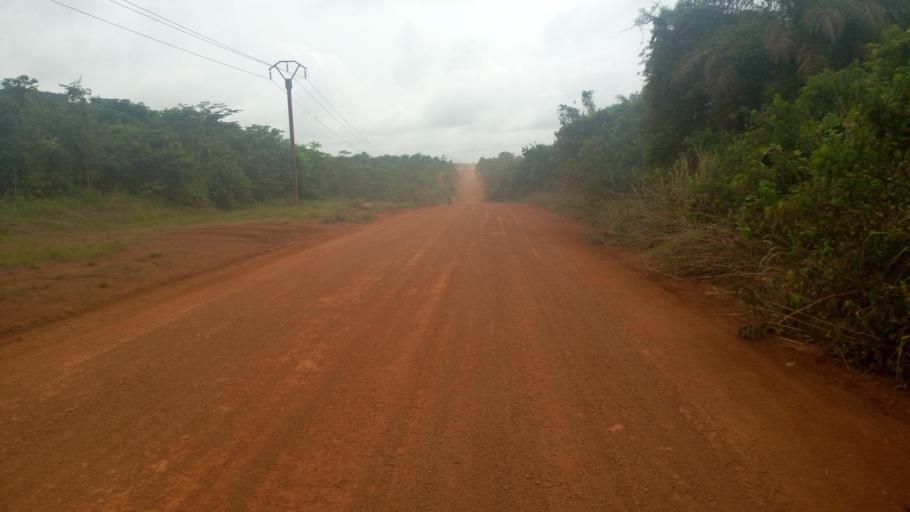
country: SL
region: Southern Province
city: Mogbwemo
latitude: 7.7091
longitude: -12.2848
